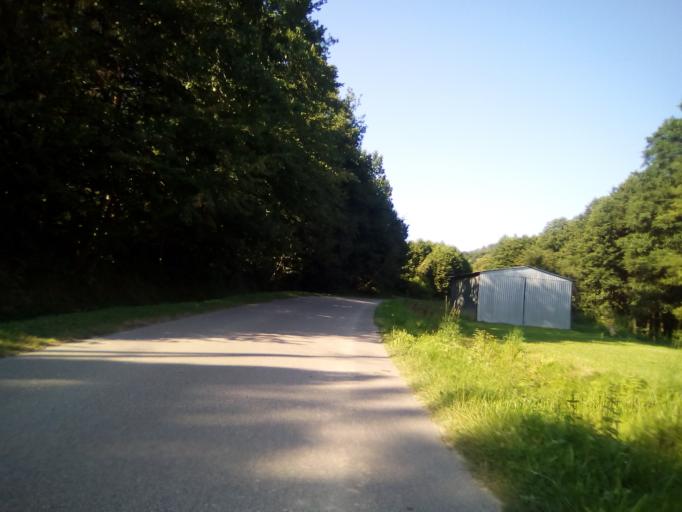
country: PL
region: Subcarpathian Voivodeship
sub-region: Powiat brzozowski
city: Domaradz
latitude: 49.8068
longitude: 21.9420
